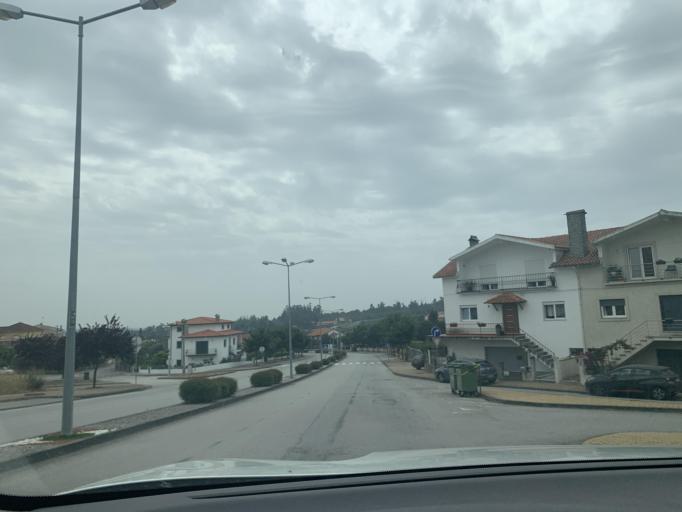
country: PT
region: Viseu
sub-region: Mangualde
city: Mangualde
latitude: 40.5913
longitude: -7.7611
